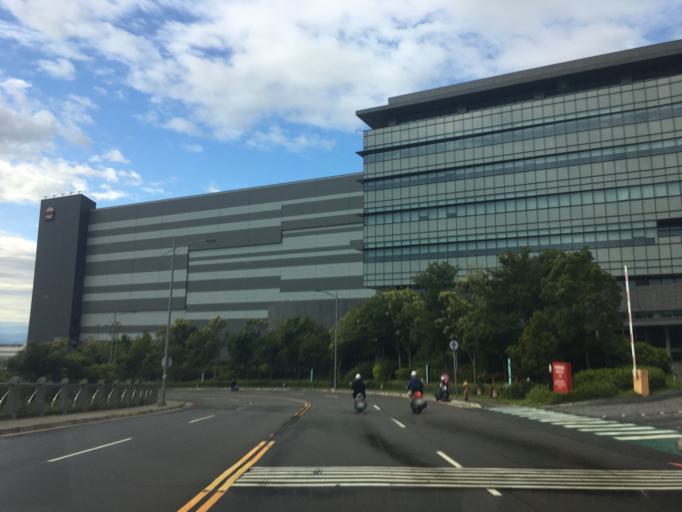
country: TW
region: Taiwan
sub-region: Taichung City
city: Taichung
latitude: 24.2110
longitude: 120.6090
